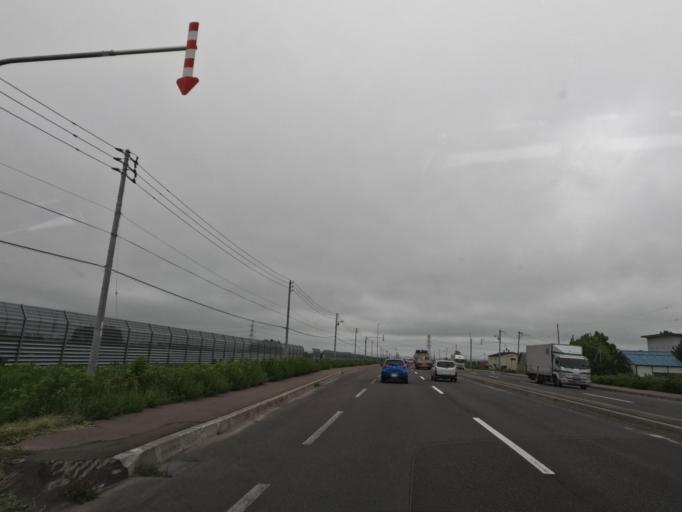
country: JP
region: Hokkaido
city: Ebetsu
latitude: 43.1545
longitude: 141.5193
